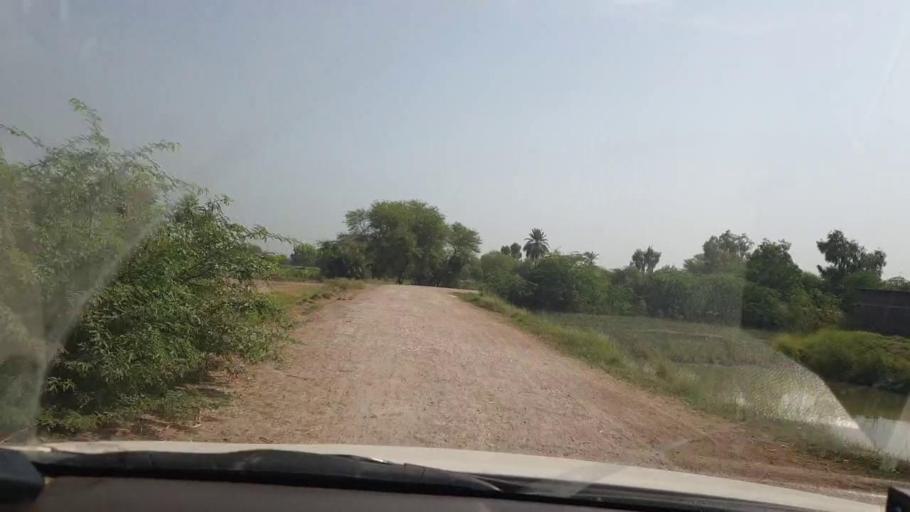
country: PK
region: Sindh
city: Chak
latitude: 27.8290
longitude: 68.7988
